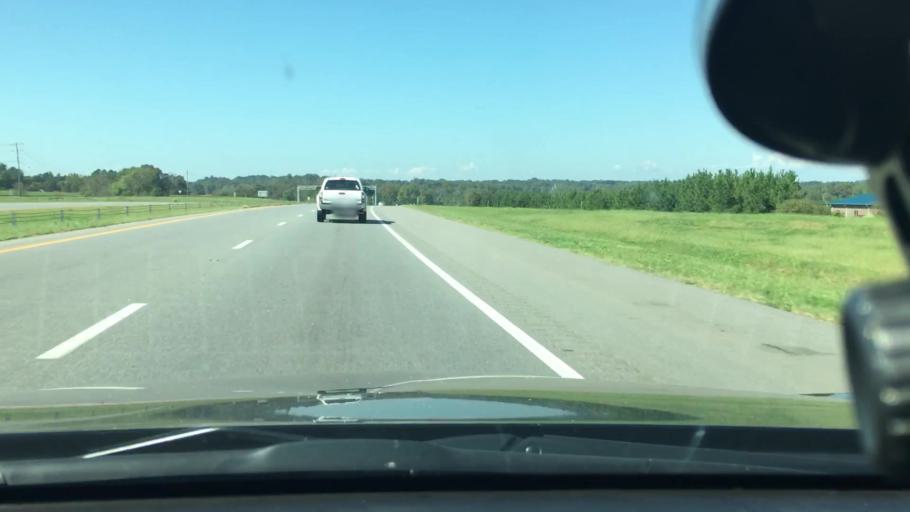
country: US
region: North Carolina
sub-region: Cleveland County
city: Boiling Springs
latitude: 35.2972
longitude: -81.6714
